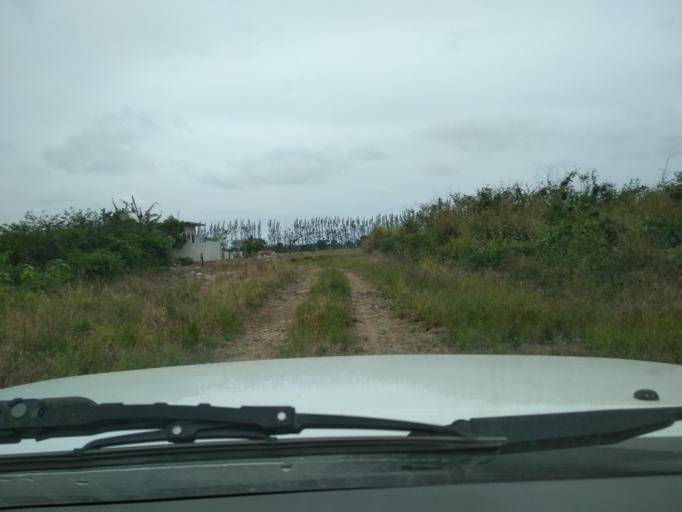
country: MX
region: Veracruz
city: Paso del Toro
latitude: 19.0457
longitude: -96.1316
